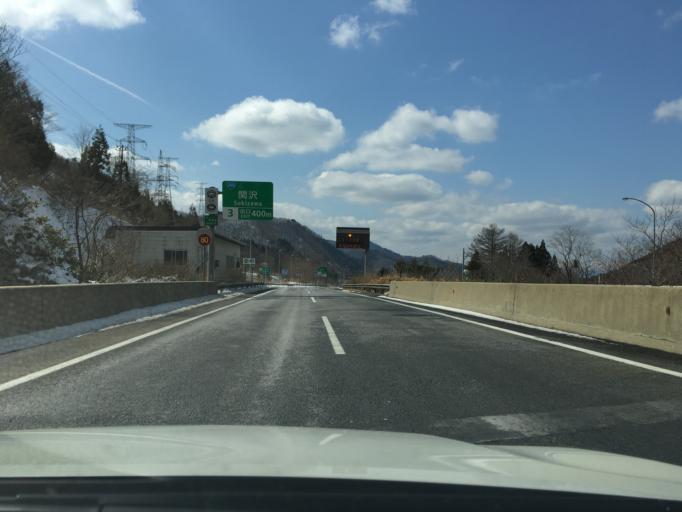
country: JP
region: Yamagata
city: Yamagata-shi
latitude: 38.2308
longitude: 140.4900
